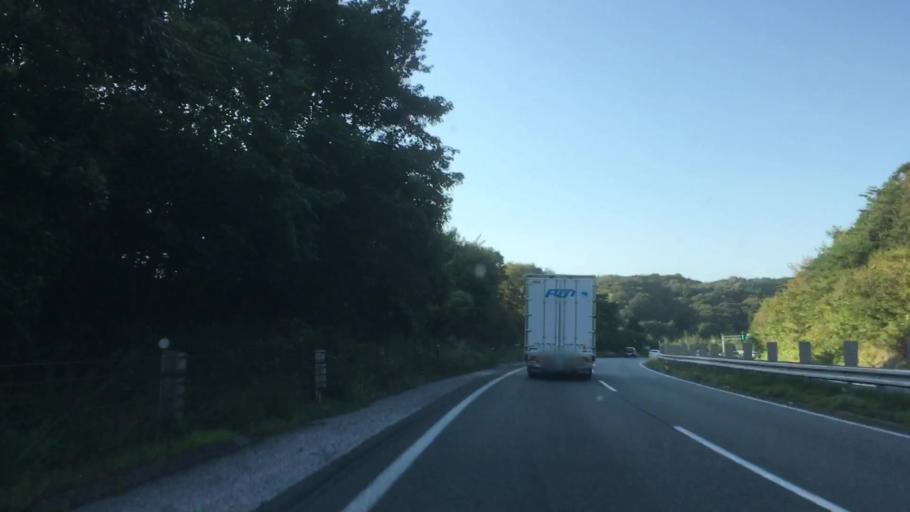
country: JP
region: Yamaguchi
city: Ogori-shimogo
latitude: 34.1624
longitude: 131.3275
